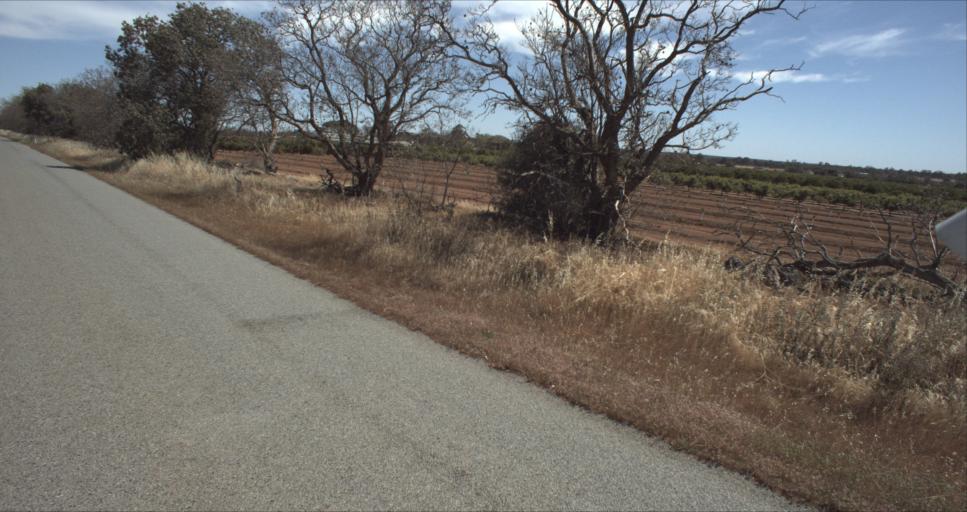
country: AU
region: New South Wales
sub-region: Leeton
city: Leeton
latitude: -34.6109
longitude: 146.4345
